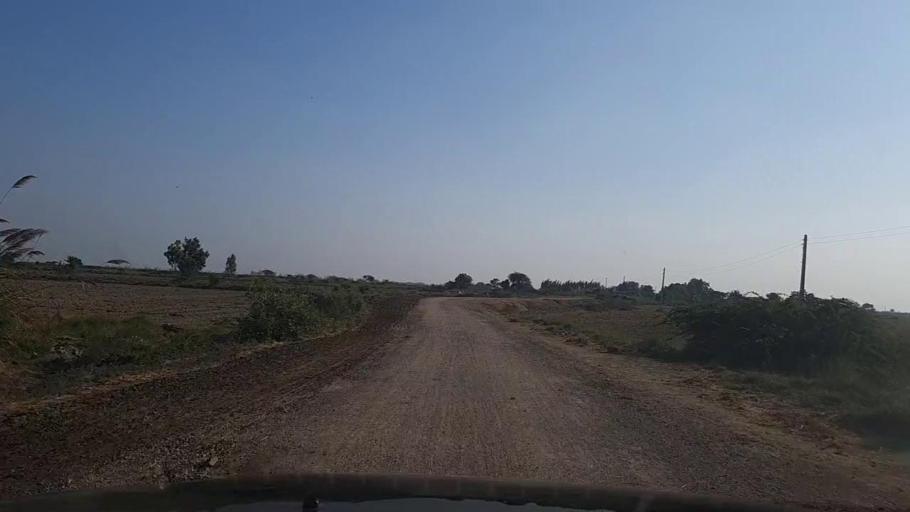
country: PK
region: Sindh
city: Gharo
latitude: 24.7078
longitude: 67.7042
